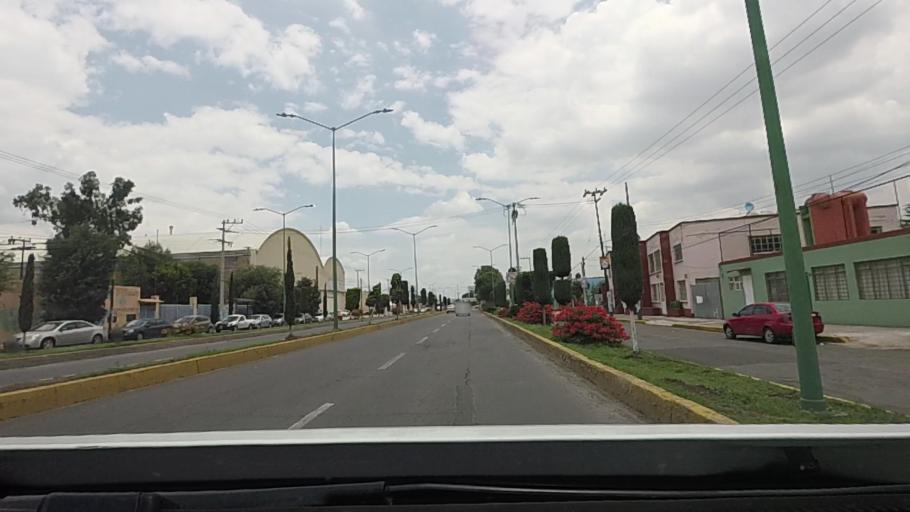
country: MX
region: Mexico
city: Chalco de Diaz Covarrubias
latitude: 19.2539
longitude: -98.8830
